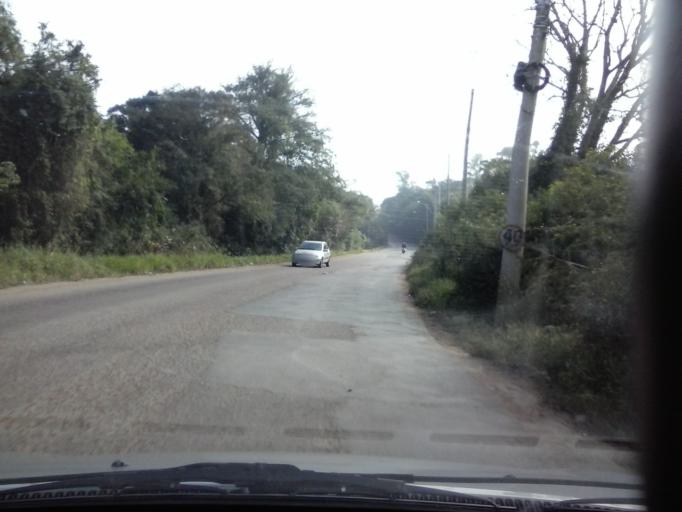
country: BR
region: Rio Grande do Sul
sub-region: Viamao
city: Viamao
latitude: -30.0508
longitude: -51.0714
